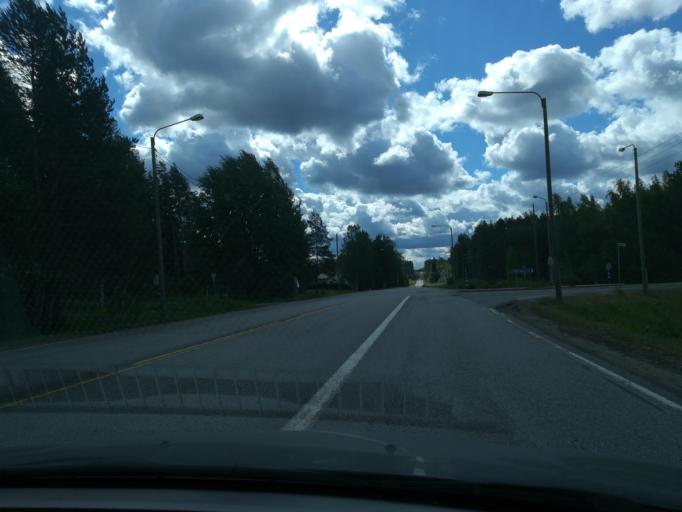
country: FI
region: Southern Savonia
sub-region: Mikkeli
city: Ristiina
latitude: 61.4536
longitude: 27.2640
